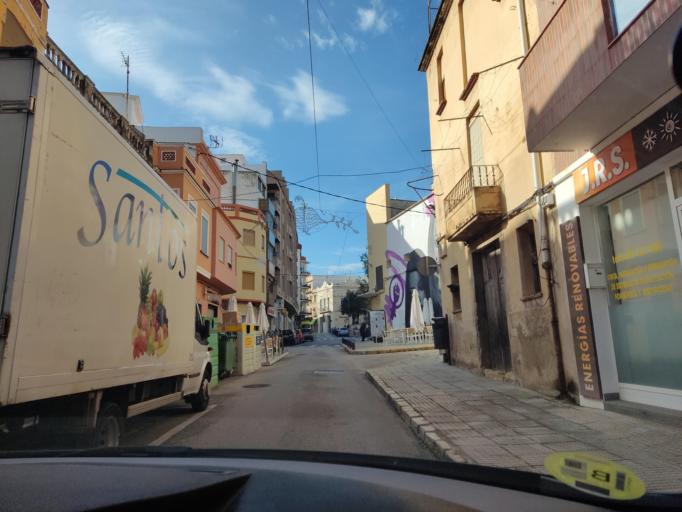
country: ES
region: Valencia
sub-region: Provincia de Alicante
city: Pego
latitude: 38.8412
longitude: -0.1147
